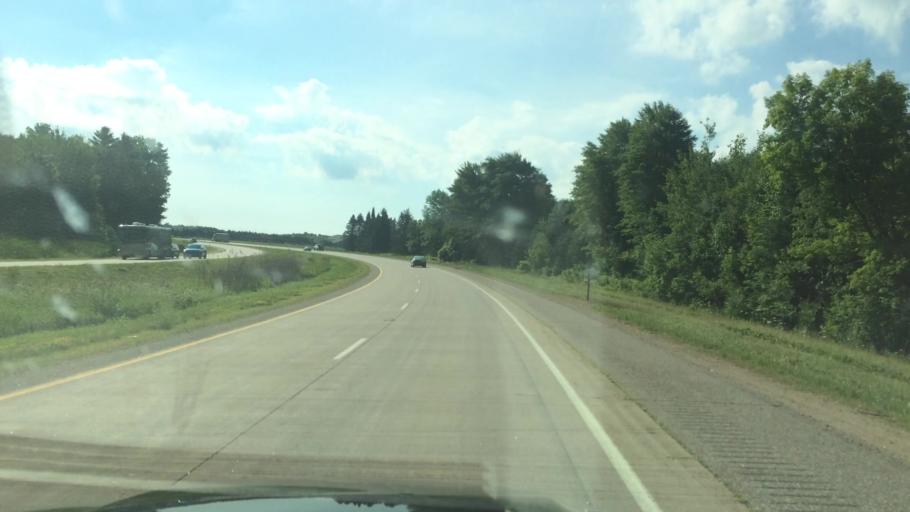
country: US
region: Wisconsin
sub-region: Shawano County
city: Wittenberg
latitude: 44.8054
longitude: -89.0343
